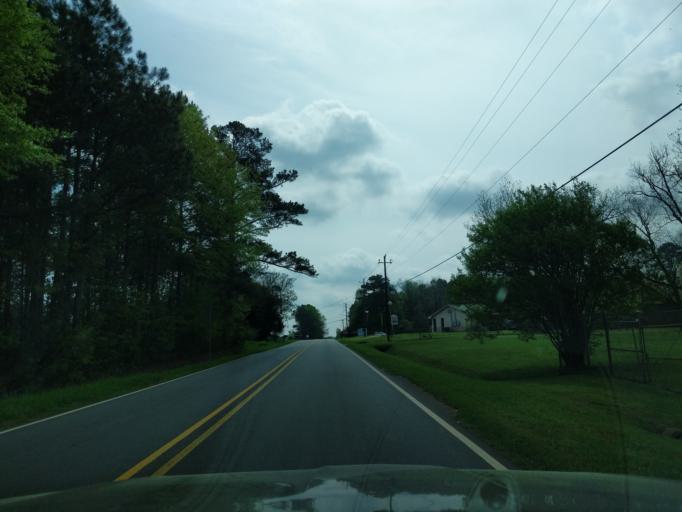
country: US
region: Georgia
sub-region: Columbia County
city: Appling
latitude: 33.6116
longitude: -82.3283
